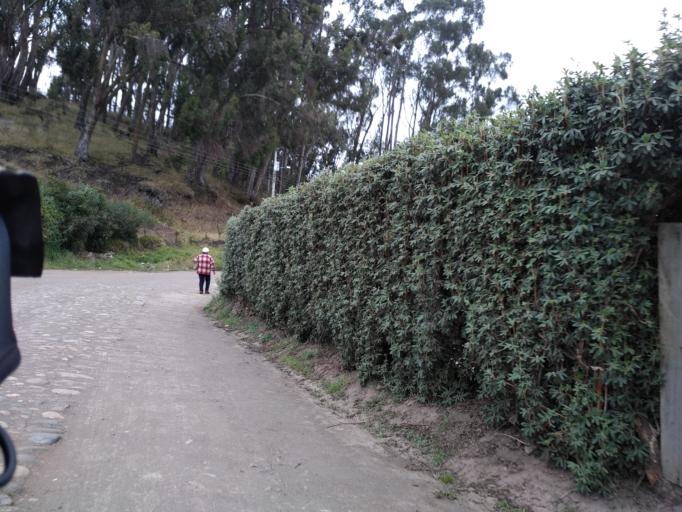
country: EC
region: Carchi
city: El Angel
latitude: 0.6350
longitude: -77.9312
